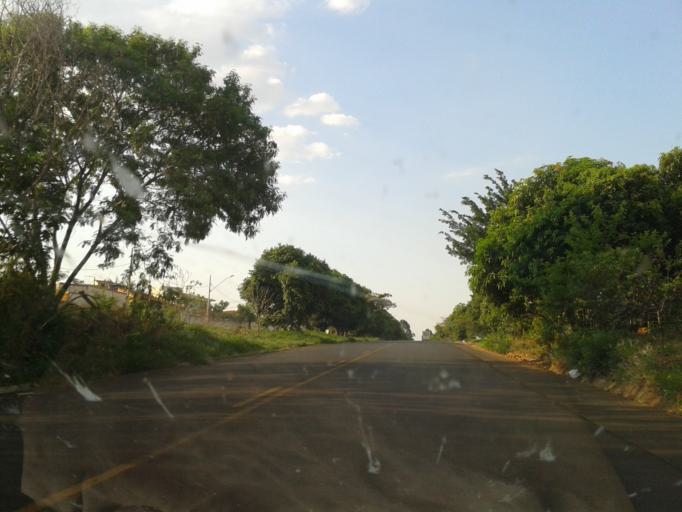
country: BR
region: Minas Gerais
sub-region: Uberlandia
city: Uberlandia
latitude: -18.9508
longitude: -48.3070
